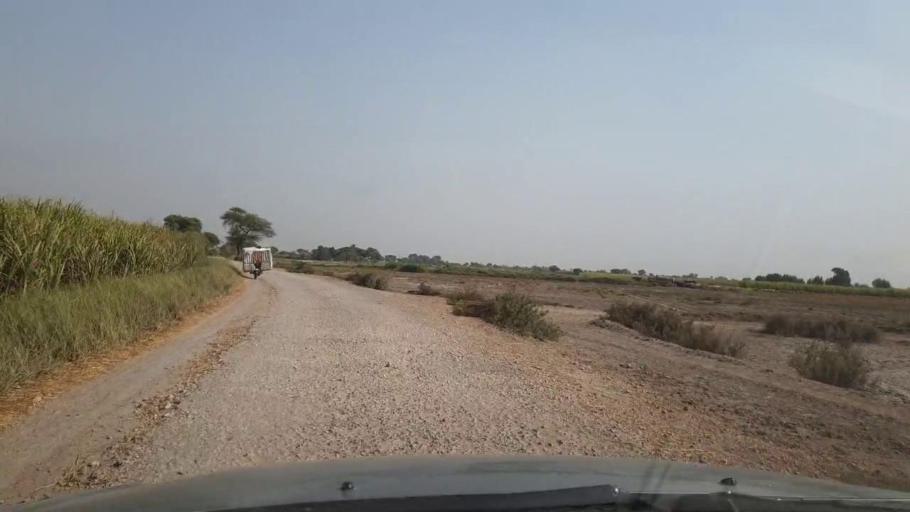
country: PK
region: Sindh
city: Bulri
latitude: 24.9119
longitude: 68.3668
